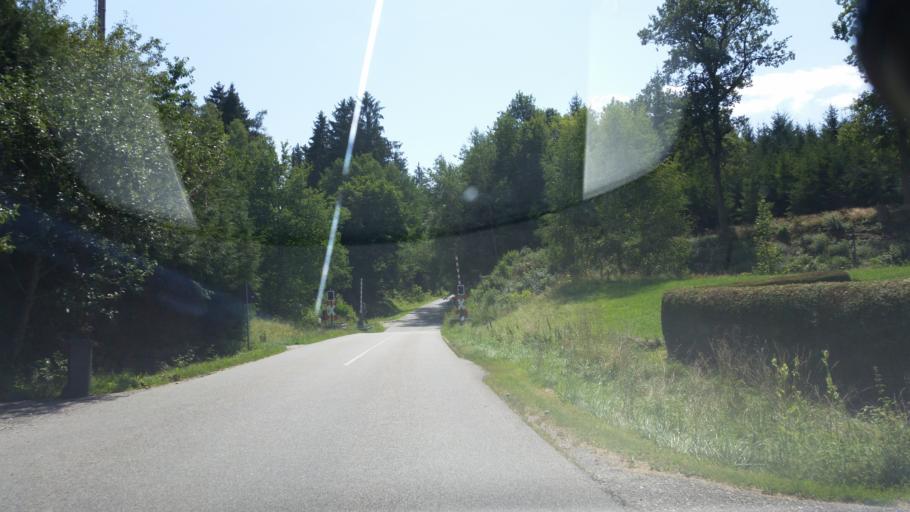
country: DE
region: Bavaria
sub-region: Lower Bavaria
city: Geisenhausen
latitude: 48.4610
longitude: 12.2770
